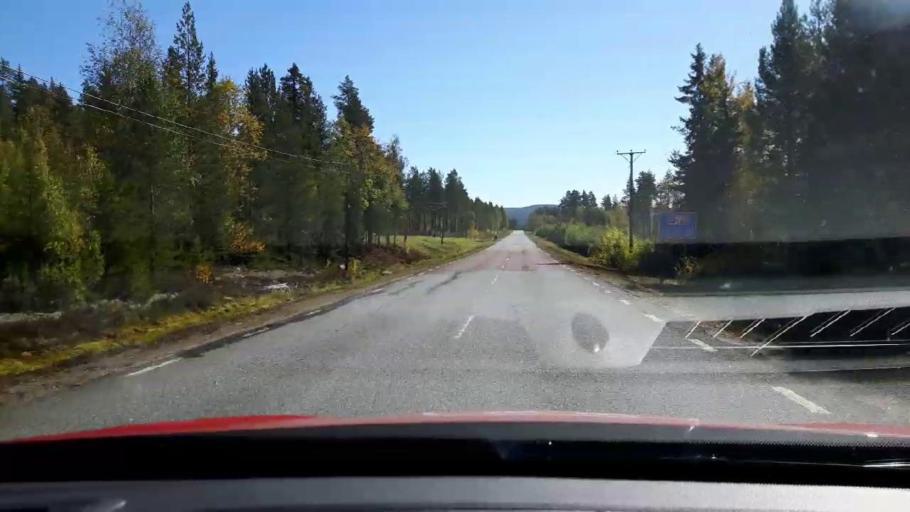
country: SE
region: Jaemtland
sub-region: Harjedalens Kommun
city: Sveg
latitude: 62.3015
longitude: 14.0619
